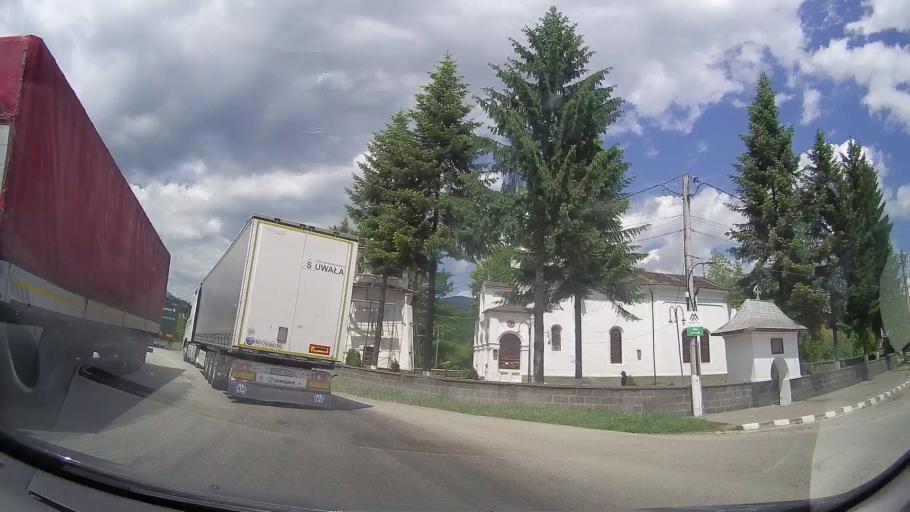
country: RO
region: Valcea
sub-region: Oras Calimanesti
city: Jiblea Veche
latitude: 45.2435
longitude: 24.3498
